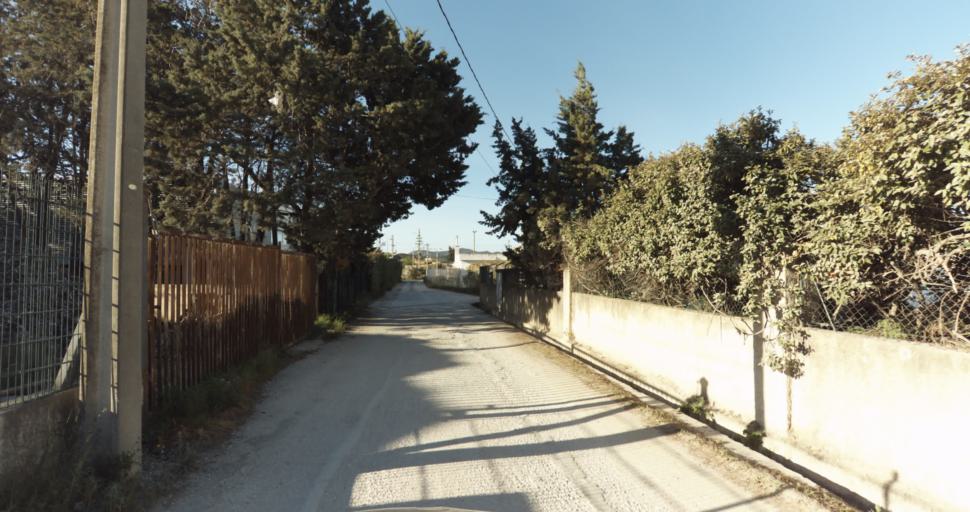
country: FR
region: Provence-Alpes-Cote d'Azur
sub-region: Departement du Var
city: Ollioules
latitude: 43.1184
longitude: 5.8571
